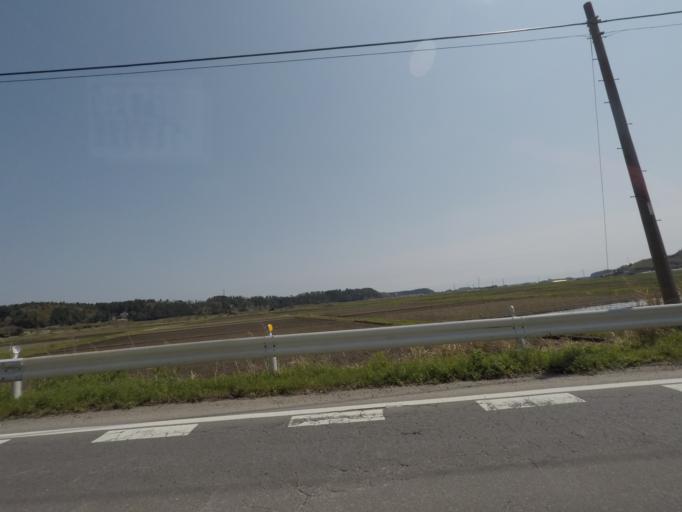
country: JP
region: Chiba
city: Yokaichiba
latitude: 35.6951
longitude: 140.4608
